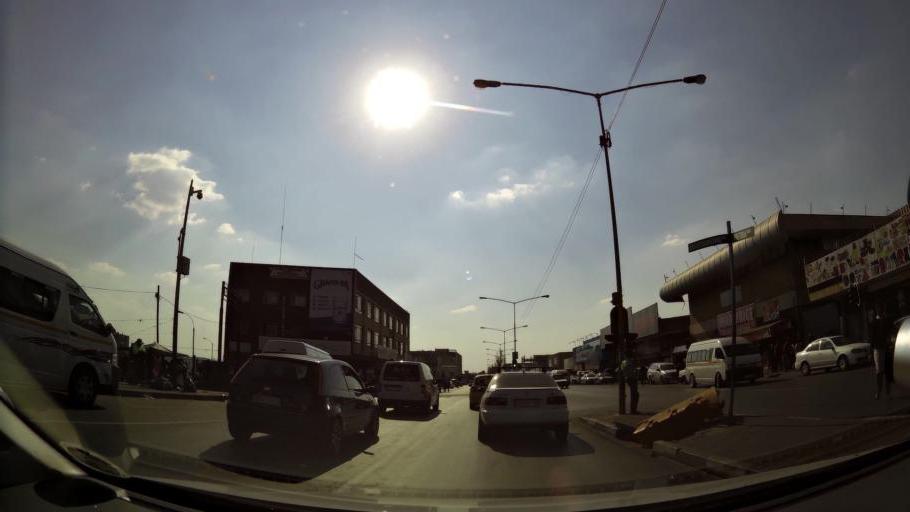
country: ZA
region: Gauteng
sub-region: City of Johannesburg Metropolitan Municipality
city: Modderfontein
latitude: -26.1064
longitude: 28.2274
